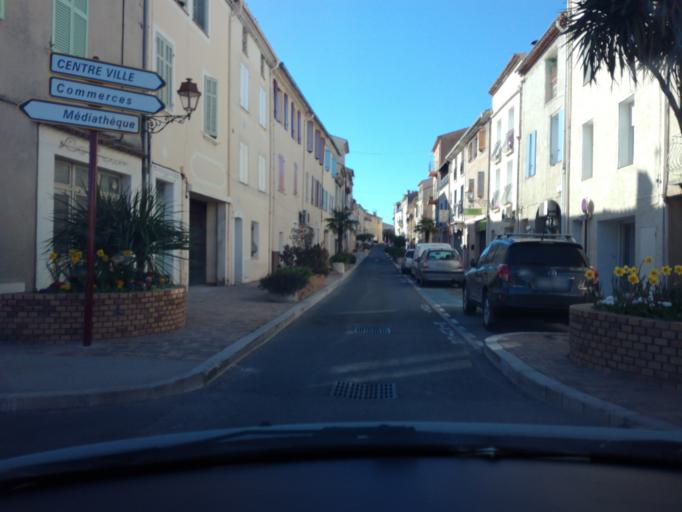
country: FR
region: Provence-Alpes-Cote d'Azur
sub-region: Departement du Var
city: Puget-sur-Argens
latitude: 43.4546
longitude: 6.6872
